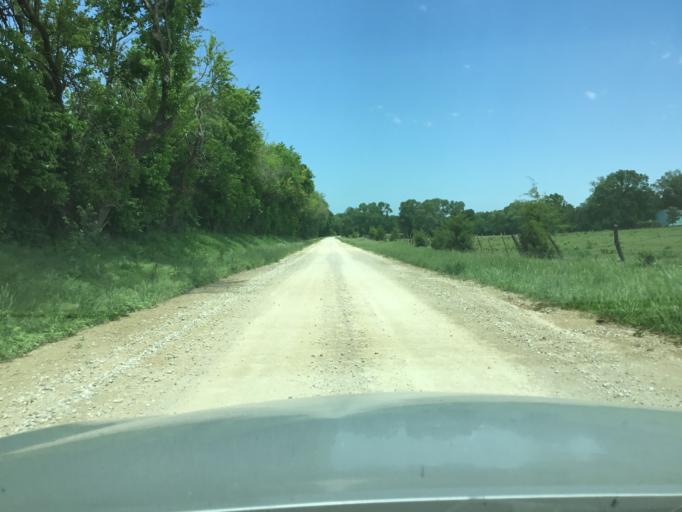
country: US
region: Kansas
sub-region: Montgomery County
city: Independence
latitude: 37.1047
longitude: -95.7830
